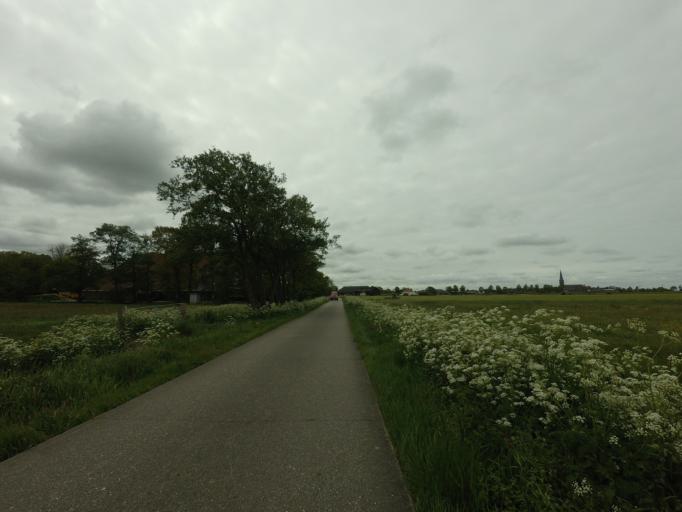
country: NL
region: Friesland
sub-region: Sudwest Fryslan
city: Workum
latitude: 52.9885
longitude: 5.4571
